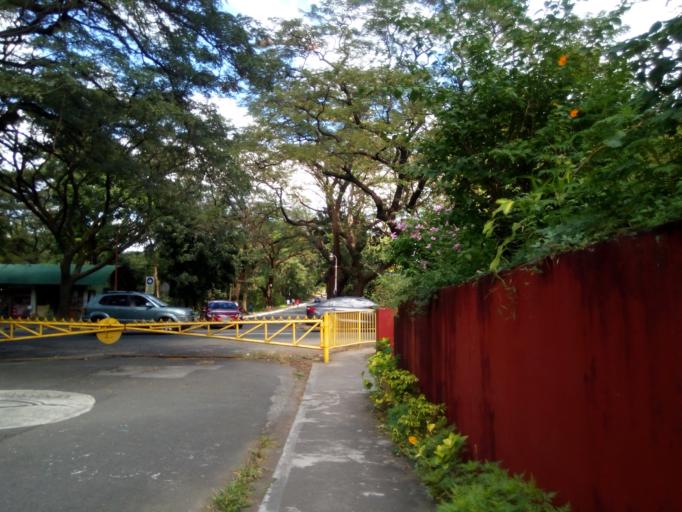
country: PH
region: Metro Manila
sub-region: Quezon City
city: Quezon City
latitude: 14.6536
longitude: 121.0687
